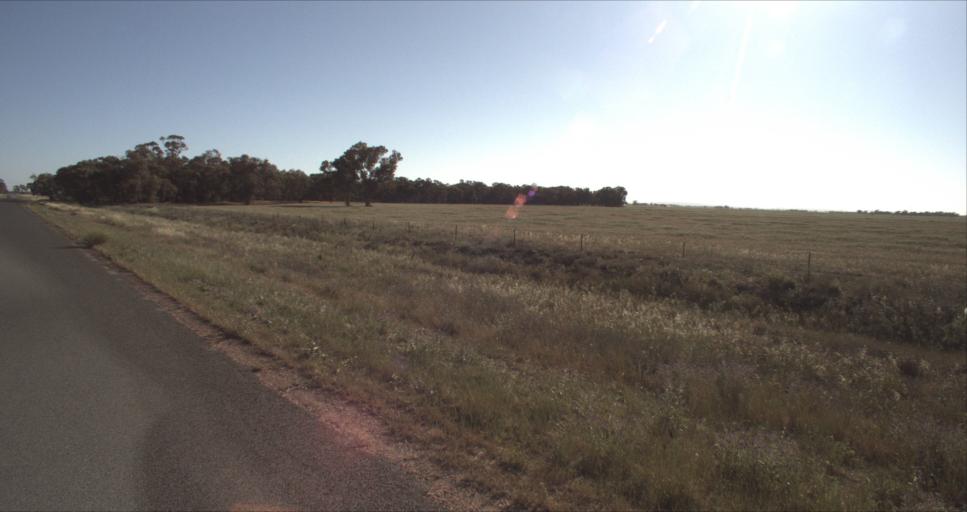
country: AU
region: New South Wales
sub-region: Leeton
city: Leeton
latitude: -34.5655
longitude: 146.2645
